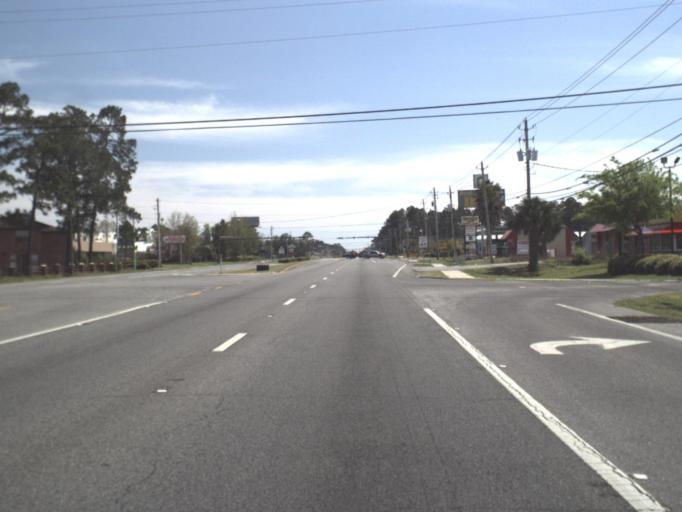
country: US
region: Florida
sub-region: Bay County
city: Lynn Haven
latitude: 30.2208
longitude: -85.6495
